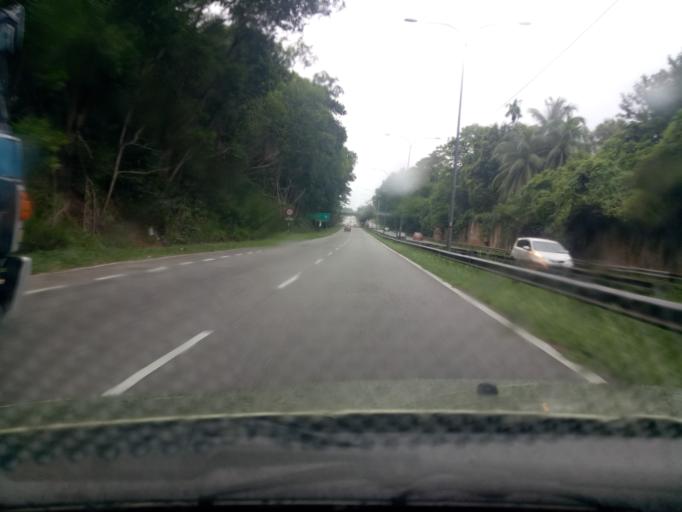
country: MY
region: Kedah
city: Sungai Petani
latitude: 5.6685
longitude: 100.5117
